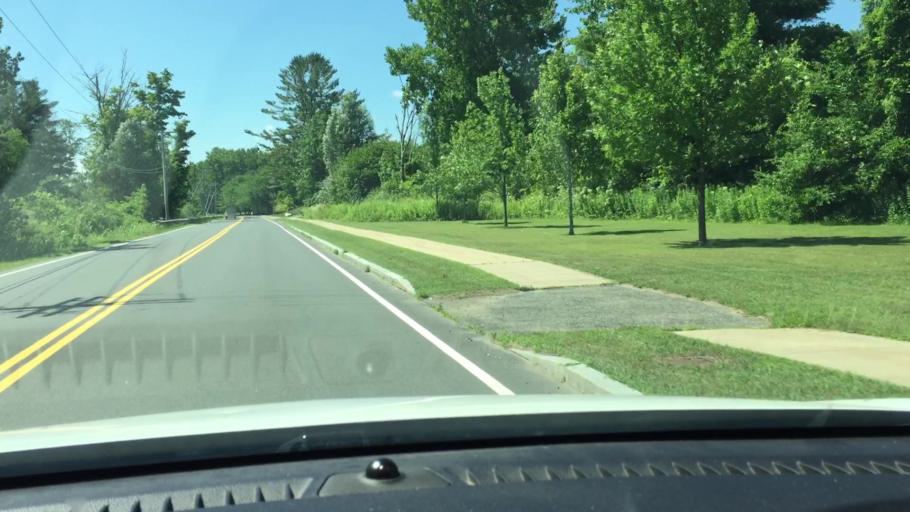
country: US
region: Massachusetts
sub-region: Berkshire County
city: Lenox
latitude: 42.3481
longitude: -73.2455
